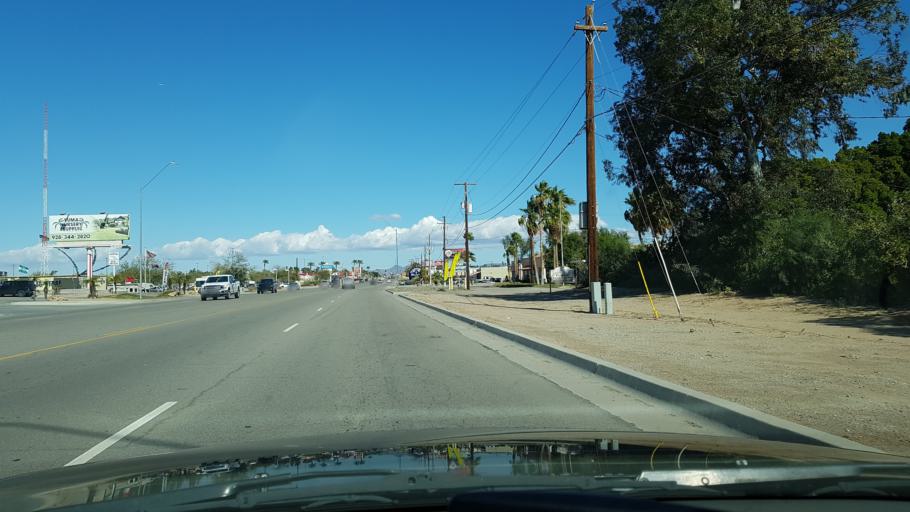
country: US
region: Arizona
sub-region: Yuma County
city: Yuma
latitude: 32.6720
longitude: -114.5987
